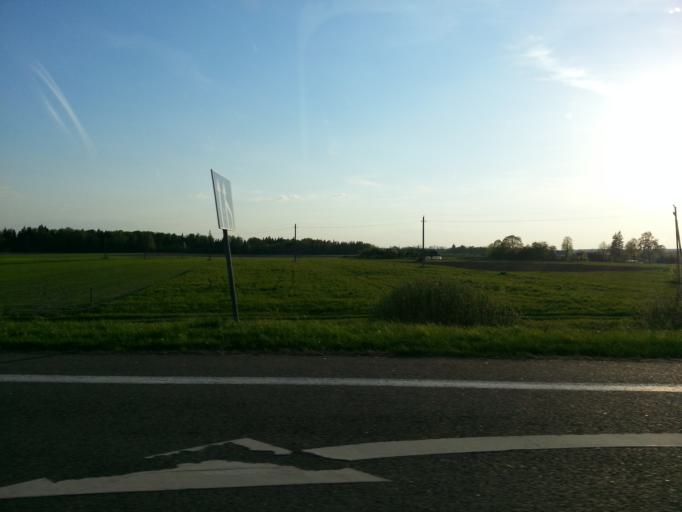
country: LT
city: Sirvintos
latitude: 55.0646
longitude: 24.8859
